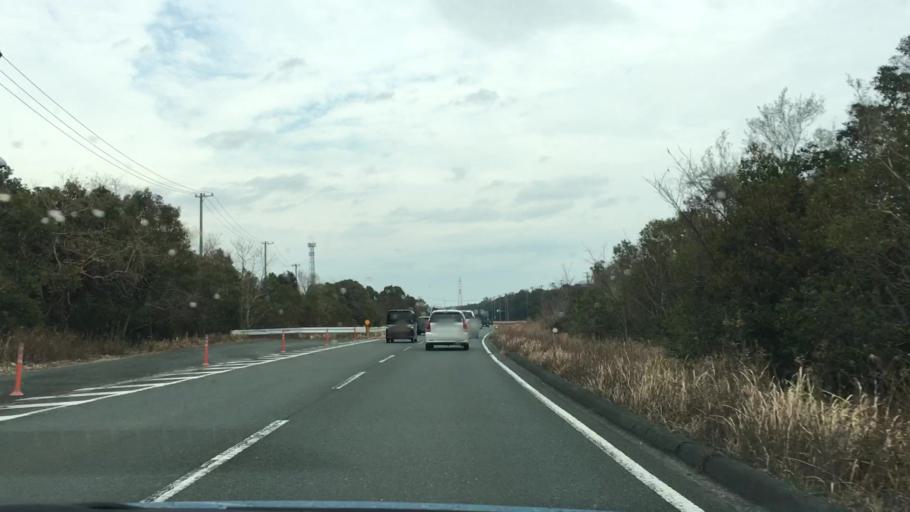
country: JP
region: Aichi
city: Tahara
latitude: 34.7043
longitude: 137.3289
